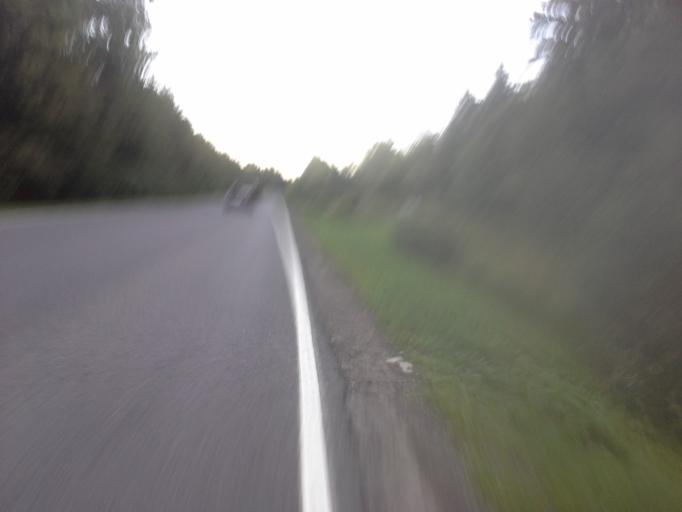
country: RU
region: Moskovskaya
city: Selyatino
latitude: 55.5096
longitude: 36.9364
